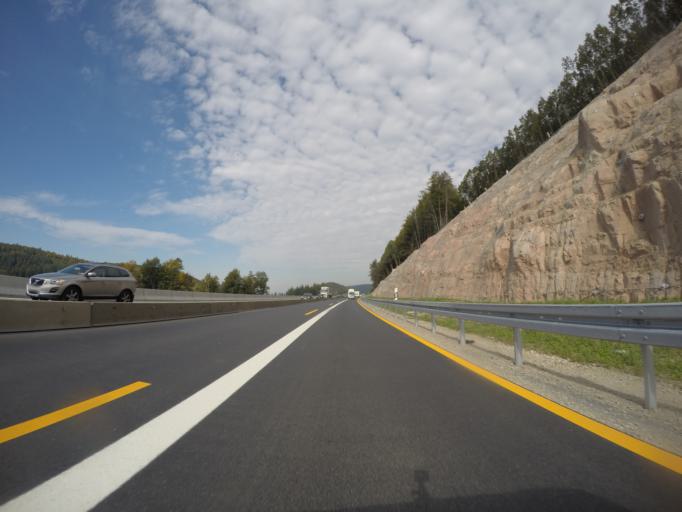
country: DE
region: Bavaria
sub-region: Regierungsbezirk Unterfranken
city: Waldaschaff
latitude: 49.9544
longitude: 9.3260
